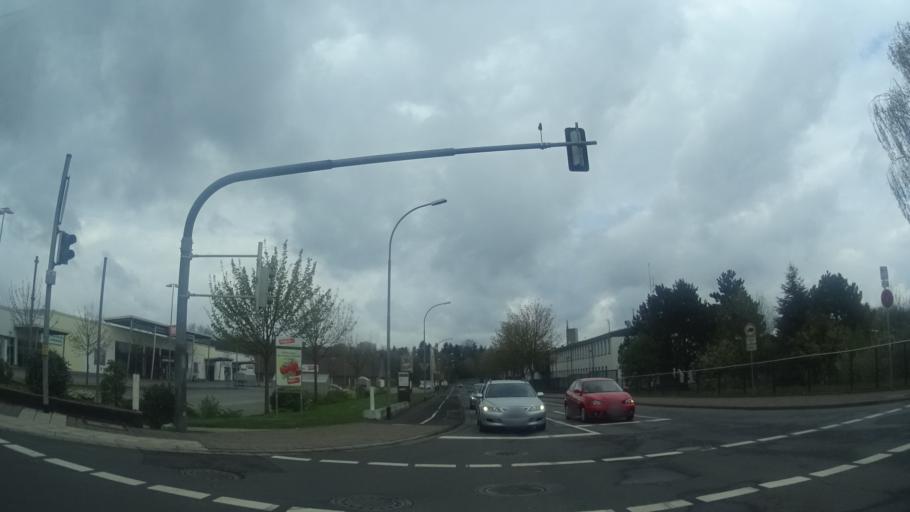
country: DE
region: Hesse
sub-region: Regierungsbezirk Giessen
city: Alsfeld
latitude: 50.7523
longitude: 9.2781
